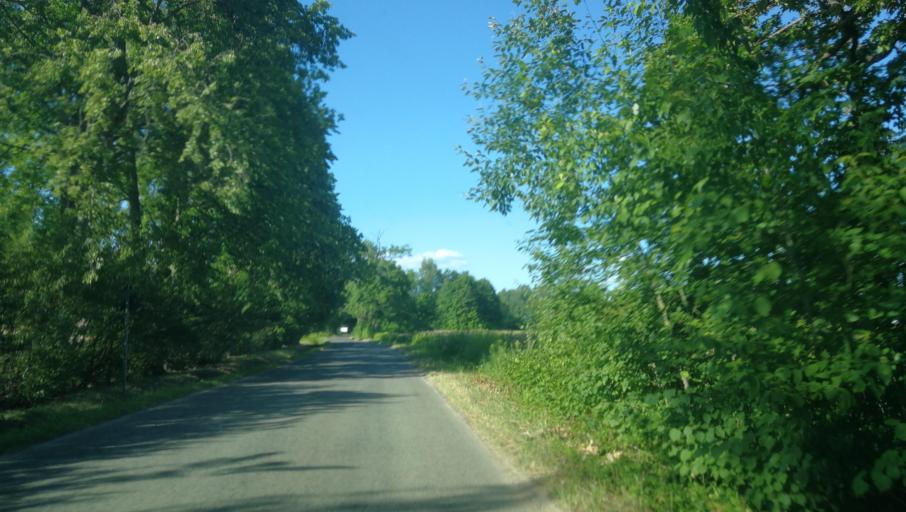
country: LV
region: Cesu Rajons
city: Cesis
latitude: 57.2929
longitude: 25.2330
